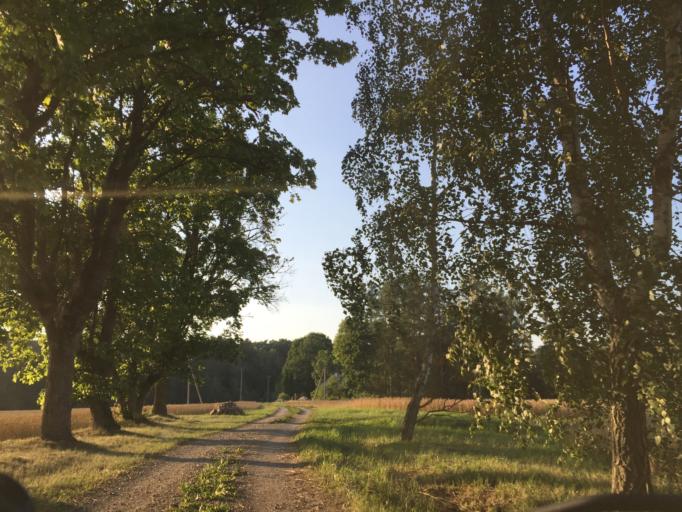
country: LV
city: Tervete
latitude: 56.4715
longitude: 23.3763
